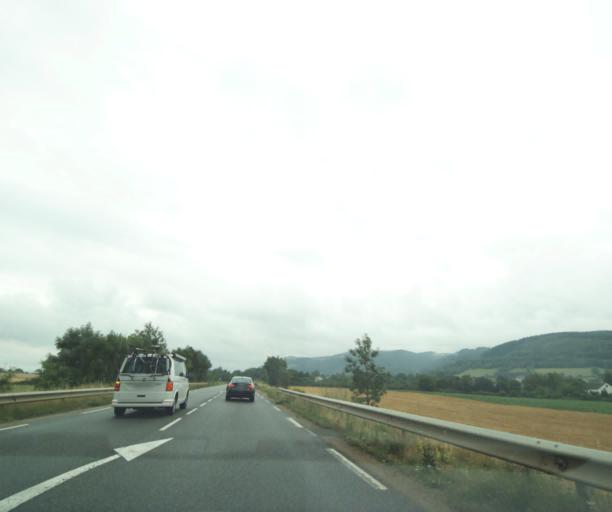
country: FR
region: Midi-Pyrenees
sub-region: Departement de l'Aveyron
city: Laissac
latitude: 44.3691
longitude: 2.8450
